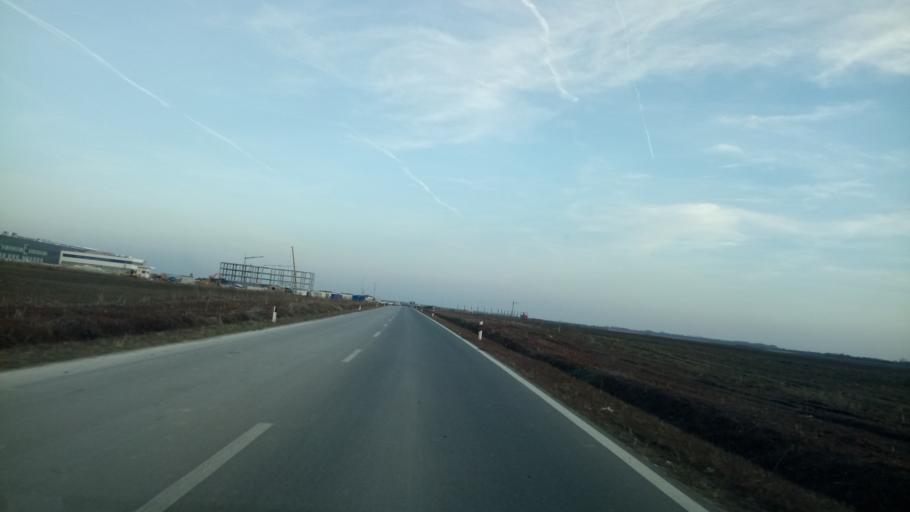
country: RS
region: Autonomna Pokrajina Vojvodina
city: Nova Pazova
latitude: 44.9633
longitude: 20.2339
